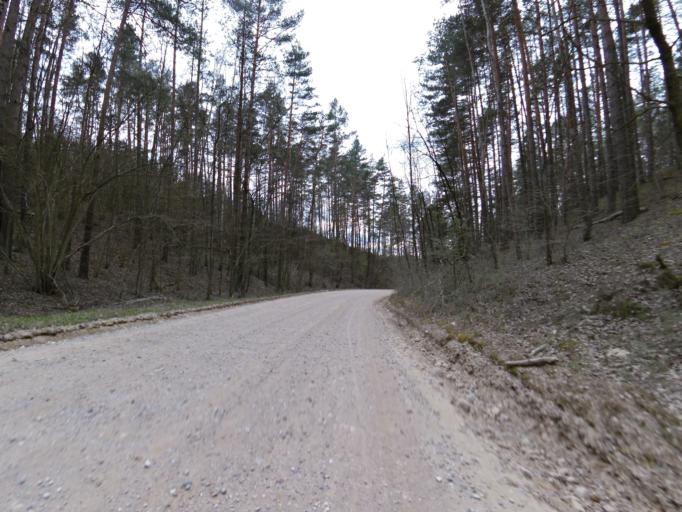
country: LT
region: Vilnius County
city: Pilaite
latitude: 54.6778
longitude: 25.1802
